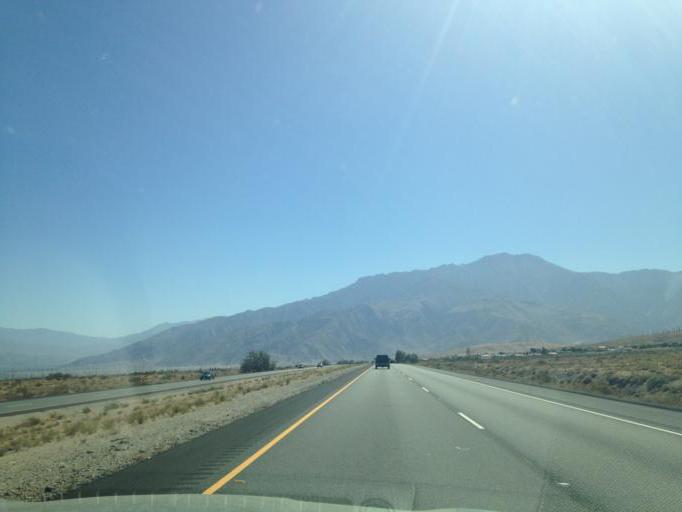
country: US
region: California
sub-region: San Bernardino County
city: Morongo Valley
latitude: 33.9702
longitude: -116.5878
